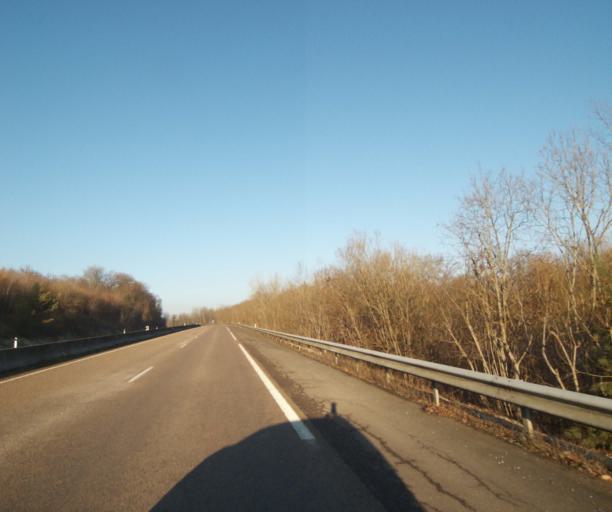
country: FR
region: Champagne-Ardenne
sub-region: Departement de la Haute-Marne
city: Chevillon
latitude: 48.5271
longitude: 5.0909
